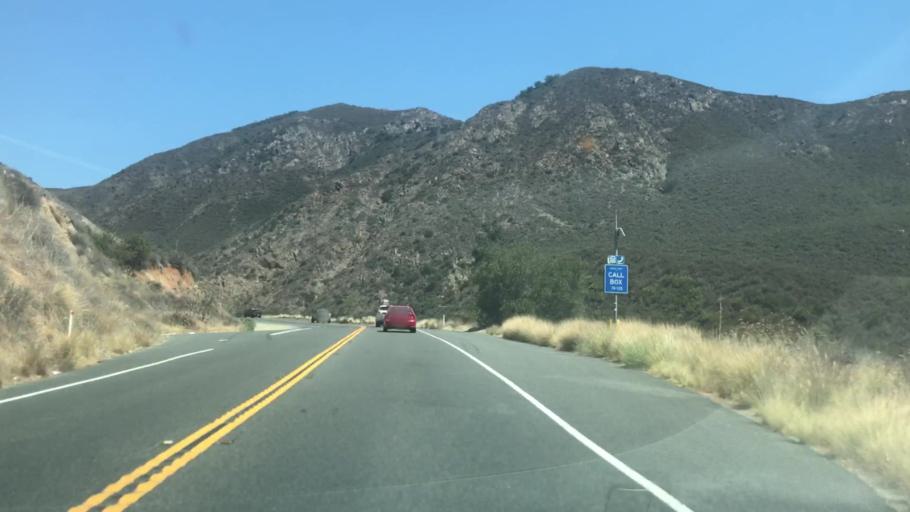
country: US
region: California
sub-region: Orange County
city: Coto De Caza
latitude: 33.5920
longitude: -117.5097
